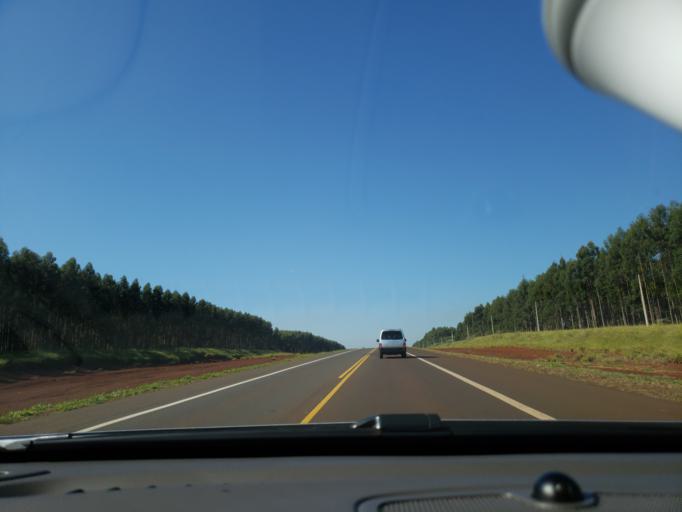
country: AR
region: Misiones
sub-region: Departamento de Capital
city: Posadas
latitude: -27.4653
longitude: -55.9558
